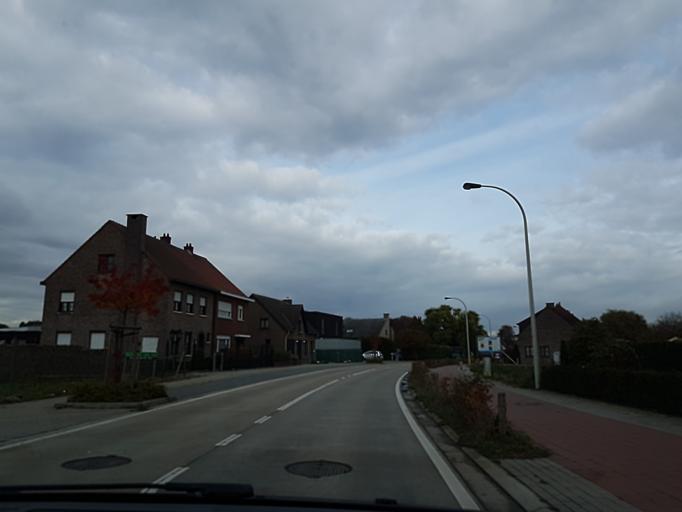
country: BE
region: Flanders
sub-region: Provincie Antwerpen
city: Ranst
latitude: 51.1832
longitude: 4.5611
